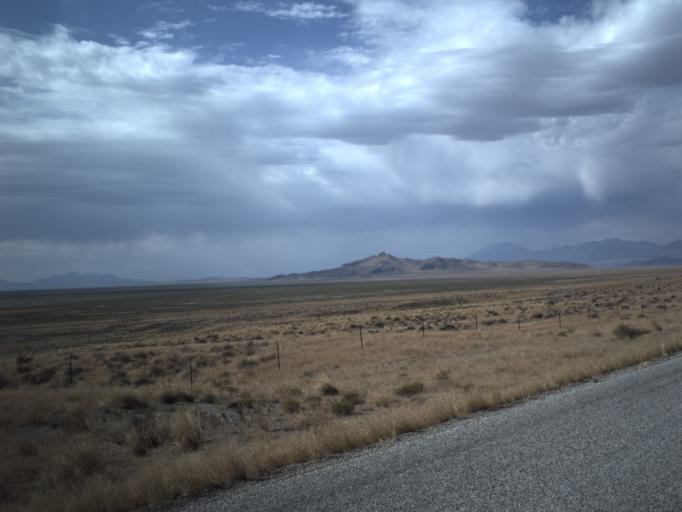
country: US
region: Utah
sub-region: Tooele County
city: Wendover
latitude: 41.4443
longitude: -113.6878
